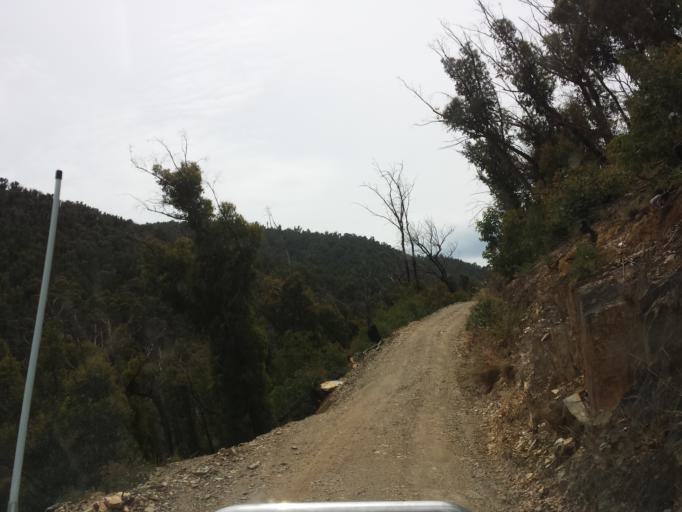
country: AU
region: Victoria
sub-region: Wellington
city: Heyfield
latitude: -37.7553
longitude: 146.5092
